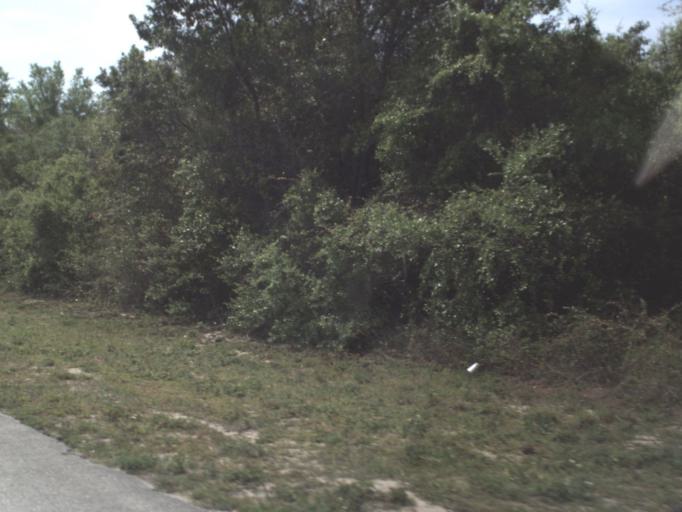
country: US
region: Florida
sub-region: Lake County
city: Astor
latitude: 29.2927
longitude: -81.6567
